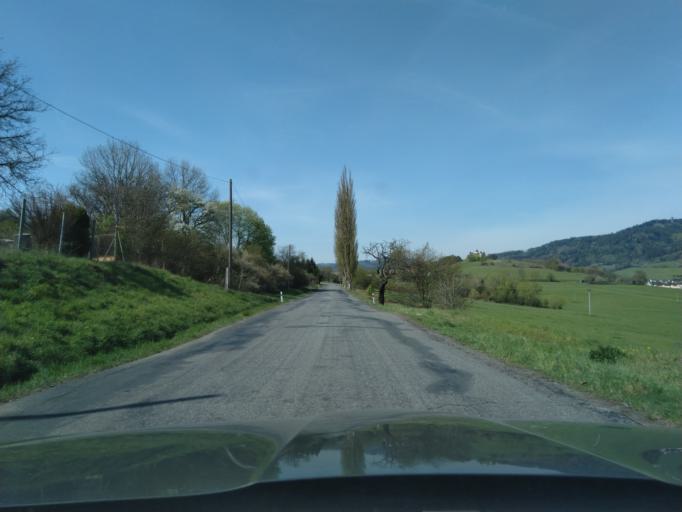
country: CZ
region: Plzensky
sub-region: Okres Klatovy
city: Susice
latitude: 49.2385
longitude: 13.5387
